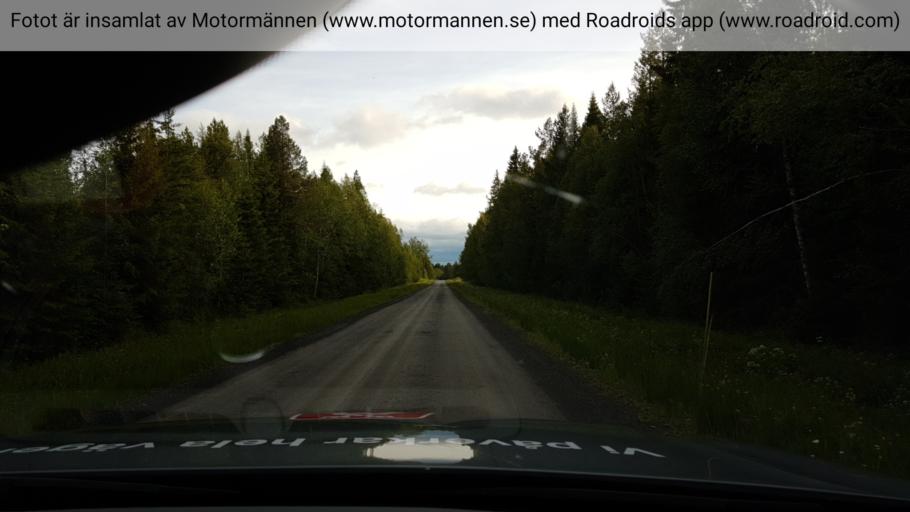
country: SE
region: Jaemtland
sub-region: Stroemsunds Kommun
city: Stroemsund
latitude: 63.7061
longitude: 15.1753
